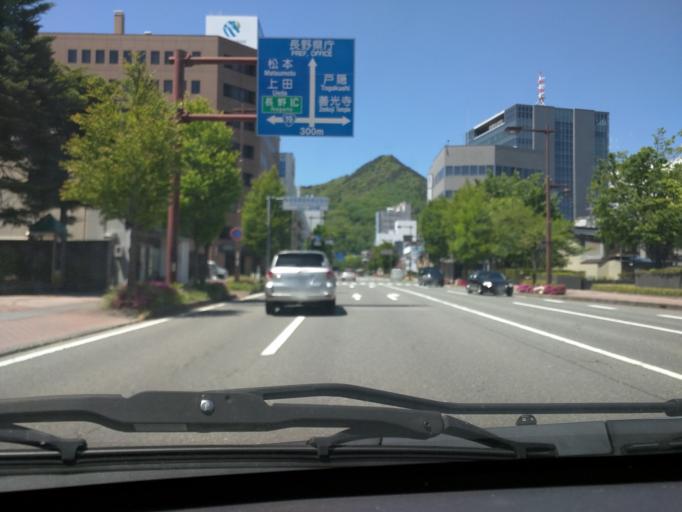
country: JP
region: Nagano
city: Nagano-shi
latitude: 36.6496
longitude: 138.1855
